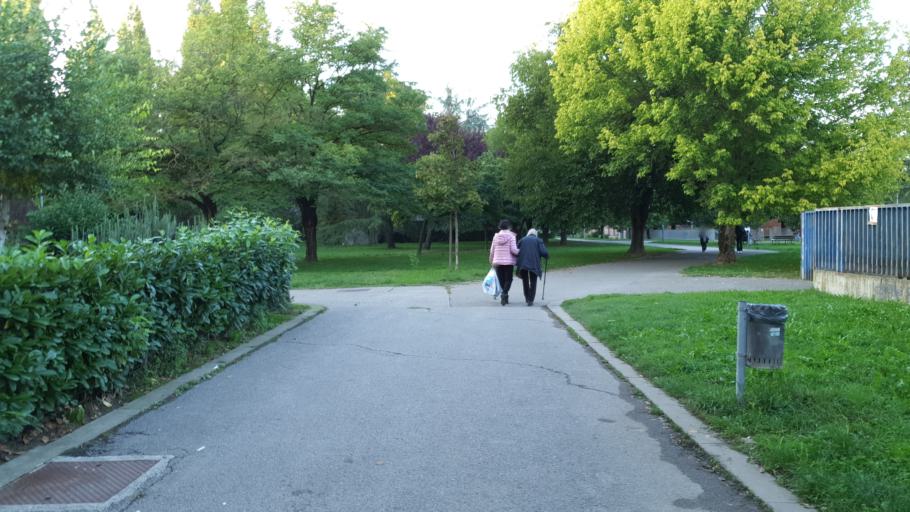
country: IT
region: Tuscany
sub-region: Province of Arezzo
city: San Giovanni Valdarno
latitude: 43.5700
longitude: 11.5272
